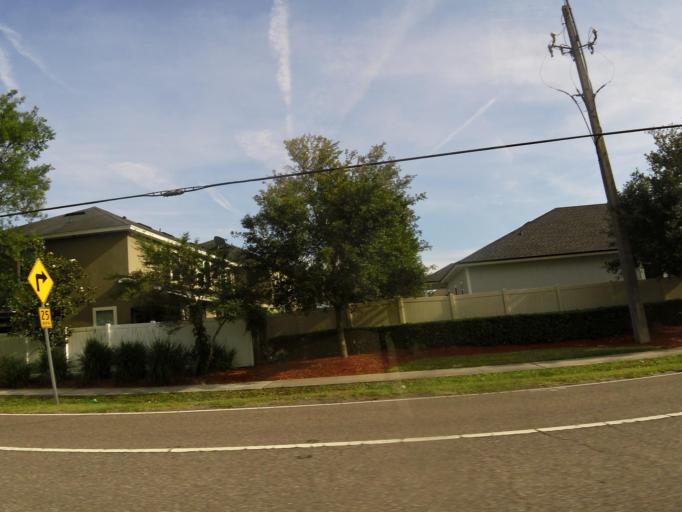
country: US
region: Florida
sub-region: Duval County
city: Jacksonville
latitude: 30.4630
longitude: -81.5643
